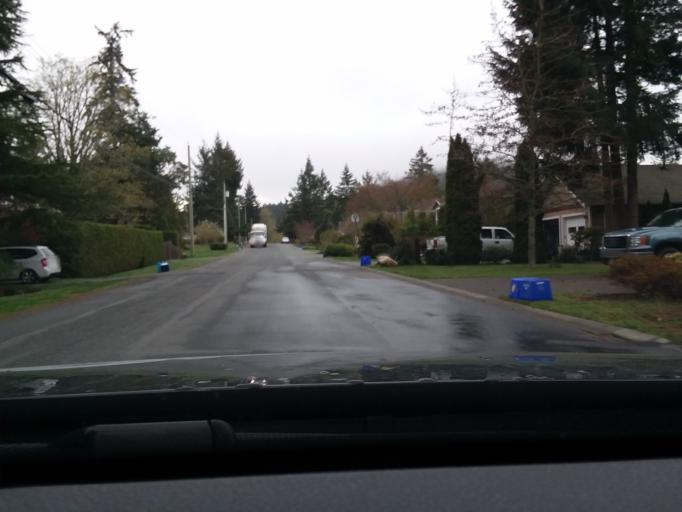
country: CA
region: British Columbia
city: North Saanich
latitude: 48.5537
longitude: -123.4008
